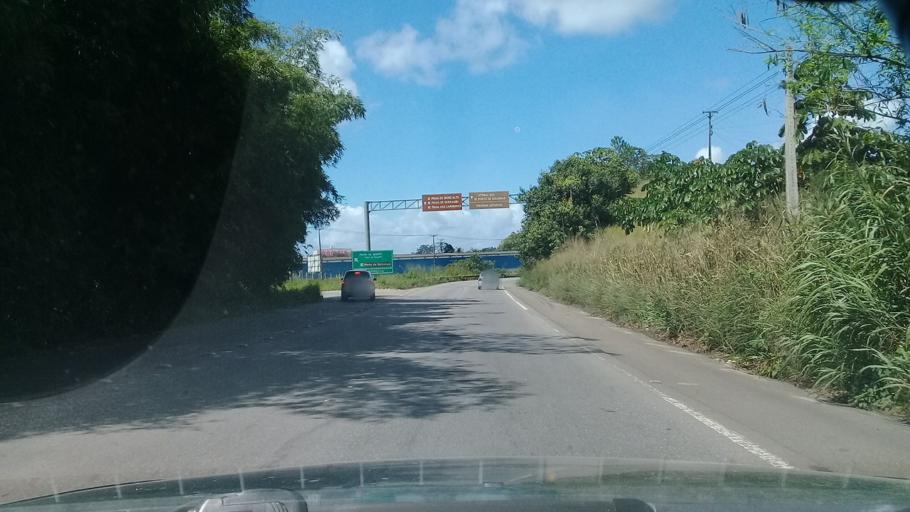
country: BR
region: Pernambuco
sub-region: Cabo De Santo Agostinho
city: Cabo
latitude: -8.3223
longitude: -35.0097
